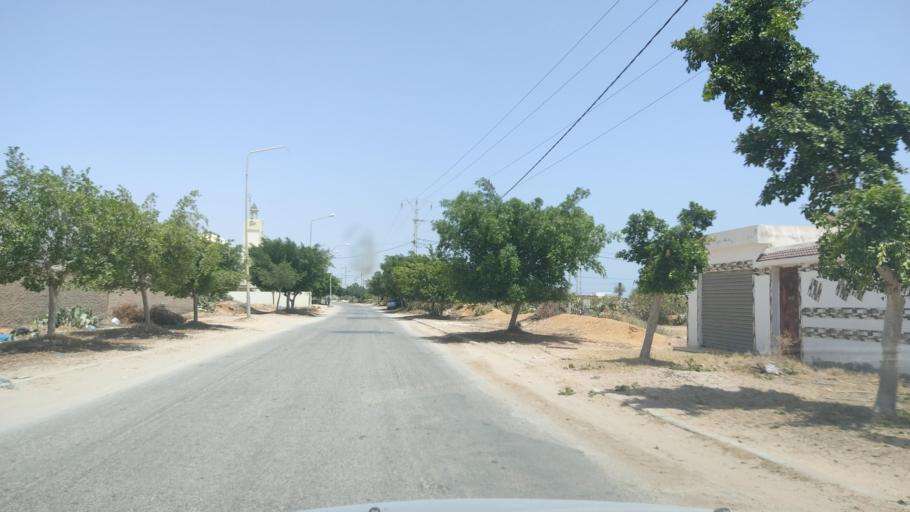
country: TN
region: Safaqis
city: Sfax
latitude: 34.6710
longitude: 10.7139
